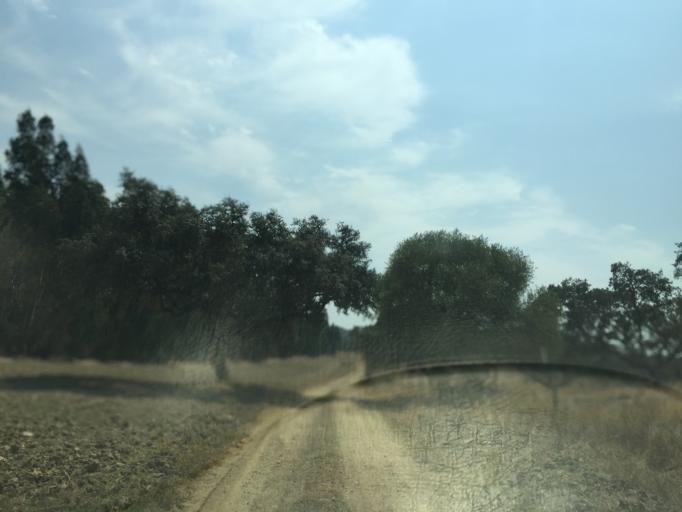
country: PT
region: Setubal
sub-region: Grandola
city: Grandola
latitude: 38.0419
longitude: -8.4800
